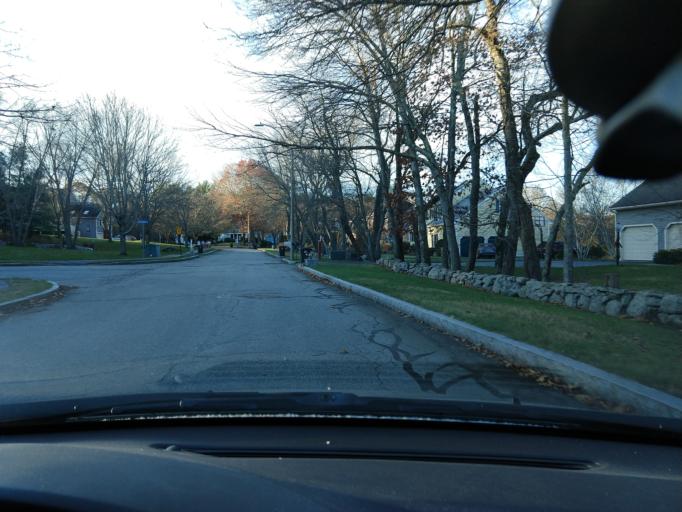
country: US
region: Massachusetts
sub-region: Middlesex County
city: Bedford
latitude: 42.4933
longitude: -71.3044
